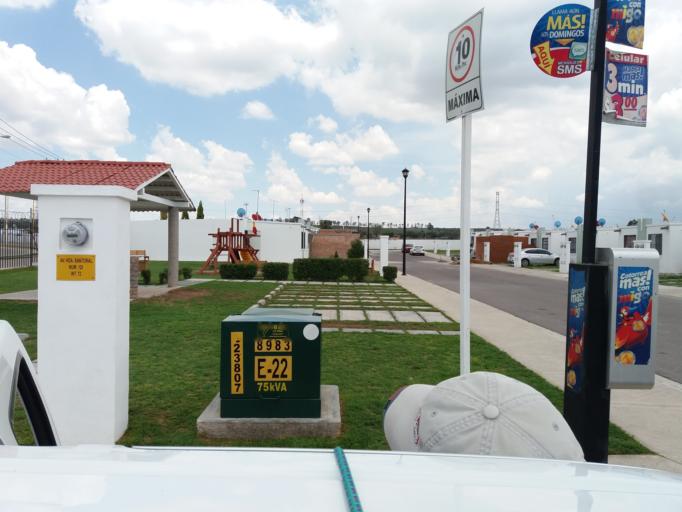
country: MX
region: Aguascalientes
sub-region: Aguascalientes
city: San Sebastian [Fraccionamiento]
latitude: 21.8044
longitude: -102.2718
